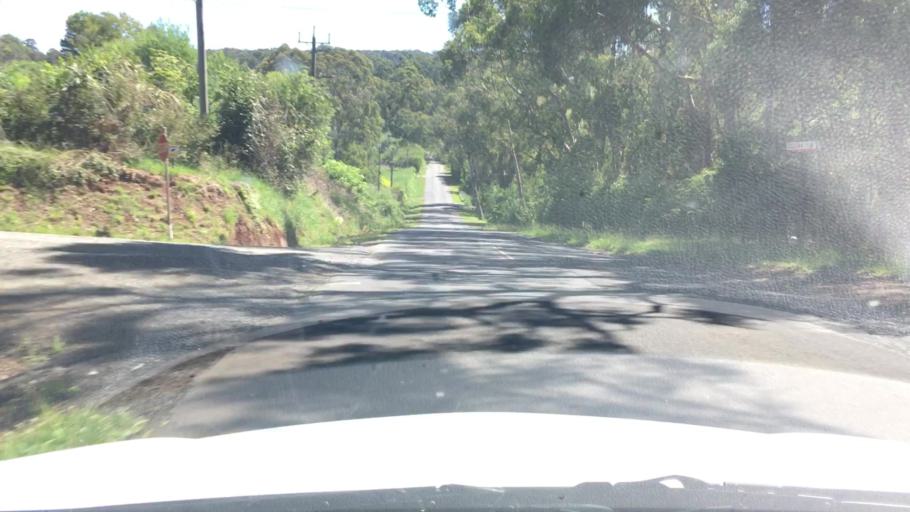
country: AU
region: Victoria
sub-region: Yarra Ranges
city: Mount Evelyn
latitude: -37.8037
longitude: 145.4126
